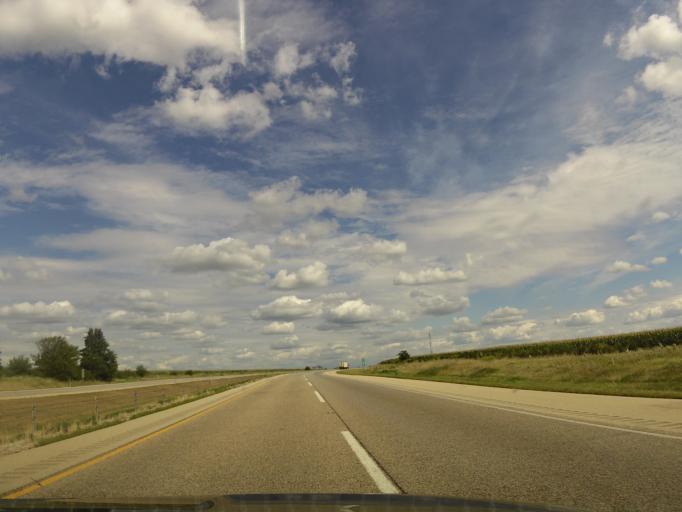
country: US
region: Illinois
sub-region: Ogle County
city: Rochelle
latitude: 41.9054
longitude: -88.9754
